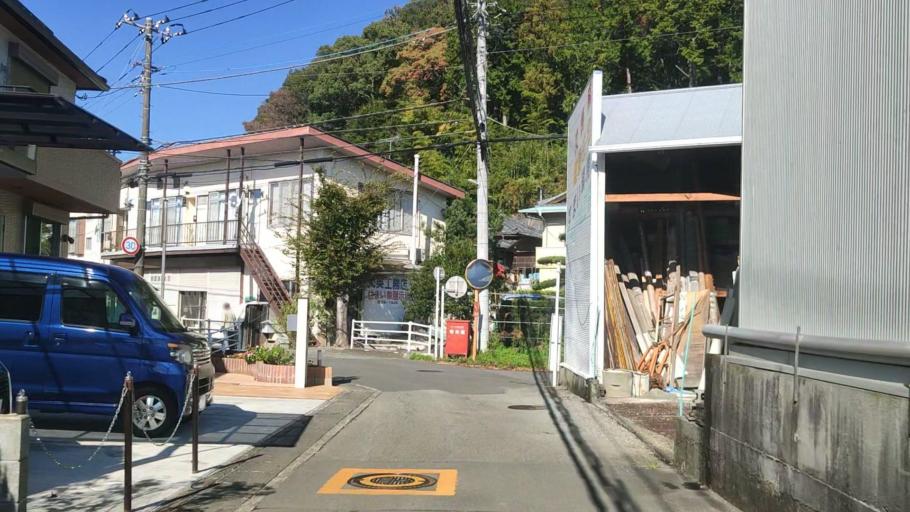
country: JP
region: Shizuoka
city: Mishima
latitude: 35.0184
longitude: 138.9505
